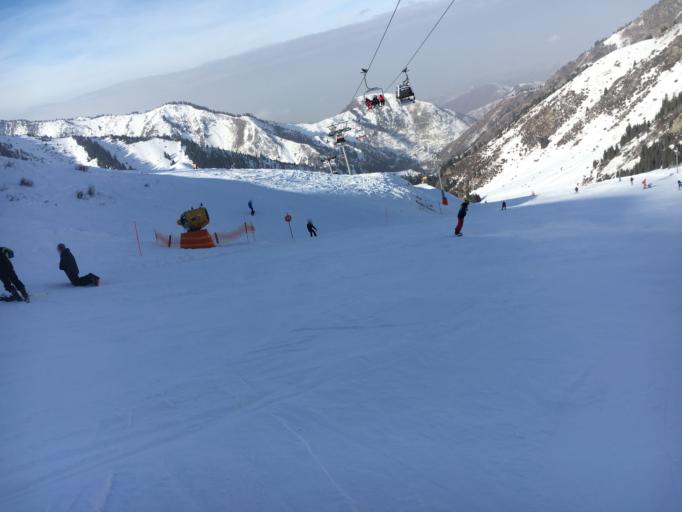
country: KZ
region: Almaty Qalasy
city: Almaty
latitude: 43.1213
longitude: 77.0952
